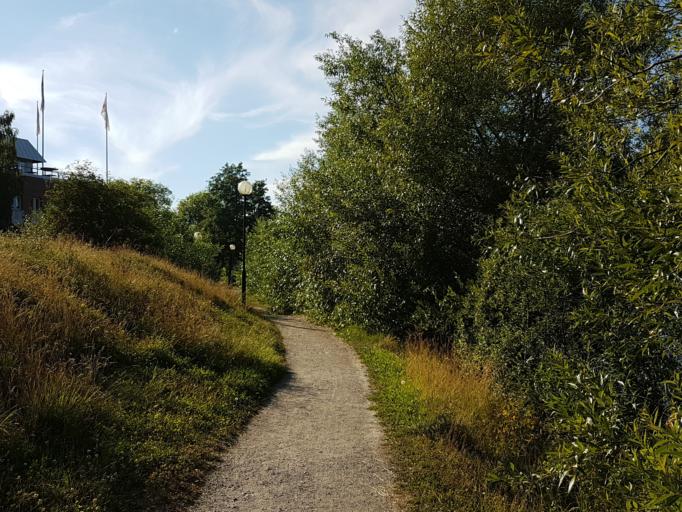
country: SE
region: Stockholm
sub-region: Solna Kommun
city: Solna
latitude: 59.3263
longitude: 17.9921
